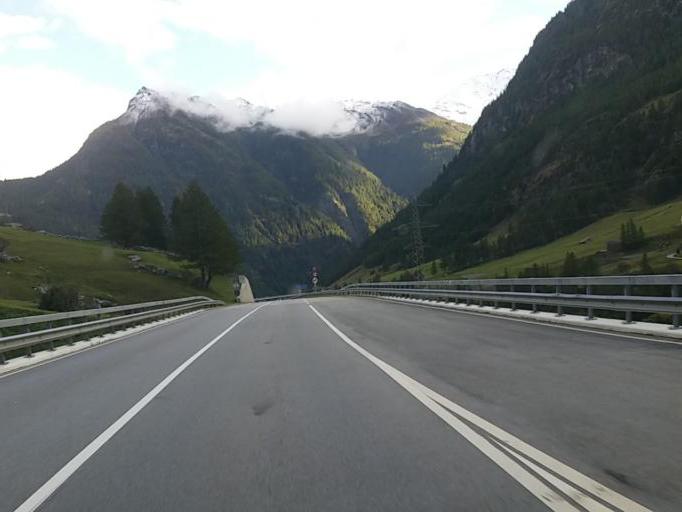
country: CH
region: Valais
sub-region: Brig District
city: Brig
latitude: 46.1987
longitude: 8.0588
